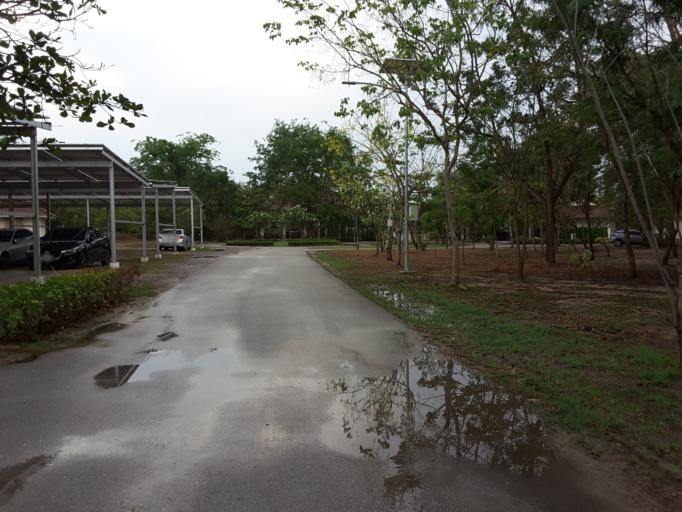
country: TH
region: Phetchaburi
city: Cha-am
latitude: 12.6871
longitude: 99.9611
